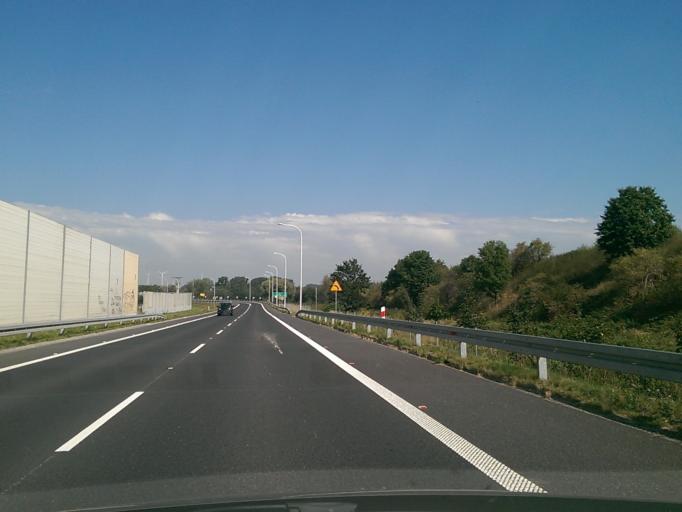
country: DE
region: Saxony
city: Zittau
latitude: 50.8976
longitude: 14.8494
